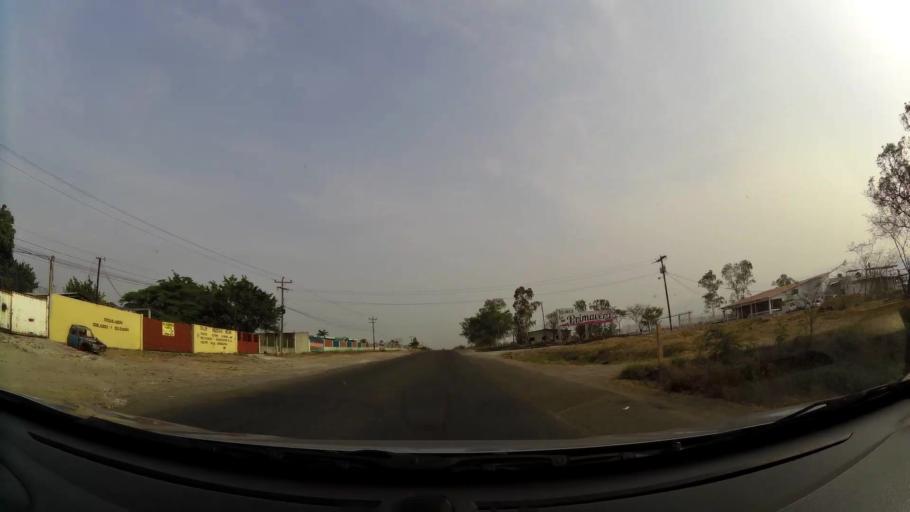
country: HN
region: Comayagua
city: Flores
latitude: 14.3073
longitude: -87.5782
